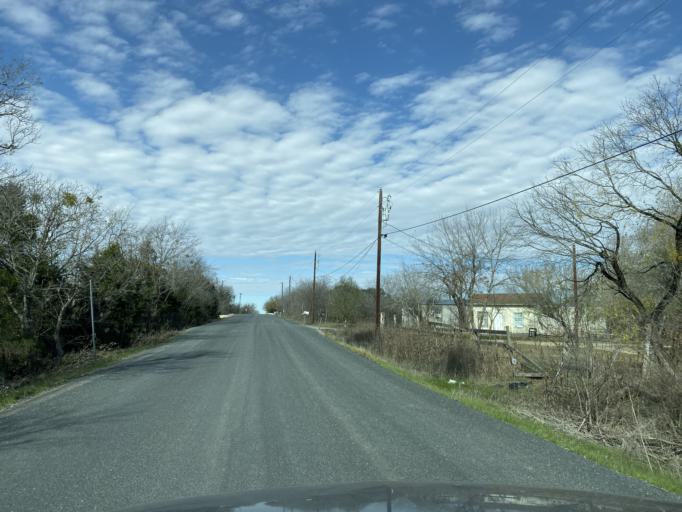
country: US
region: Texas
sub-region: Travis County
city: Onion Creek
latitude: 30.0823
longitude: -97.7006
